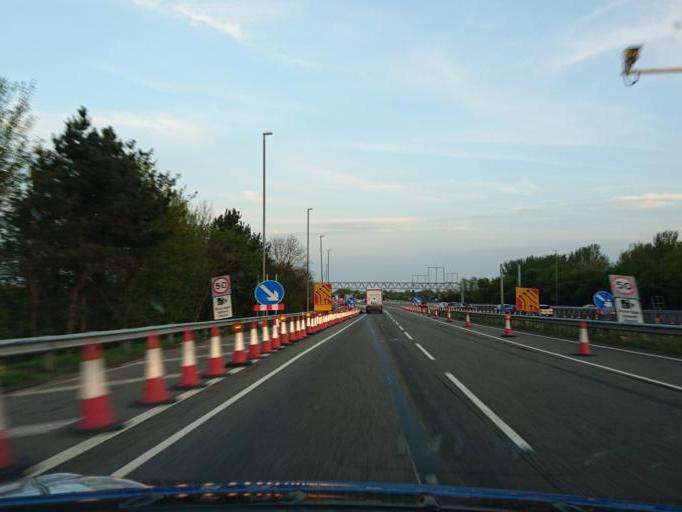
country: GB
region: England
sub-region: Leicestershire
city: Lutterworth
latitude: 52.3981
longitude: -1.1735
